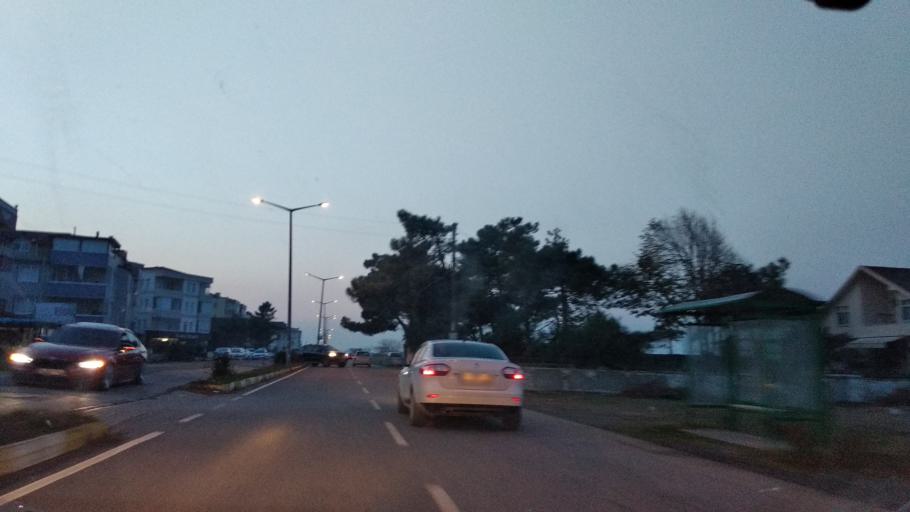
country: TR
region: Sakarya
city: Karasu
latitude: 41.0952
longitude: 30.7326
